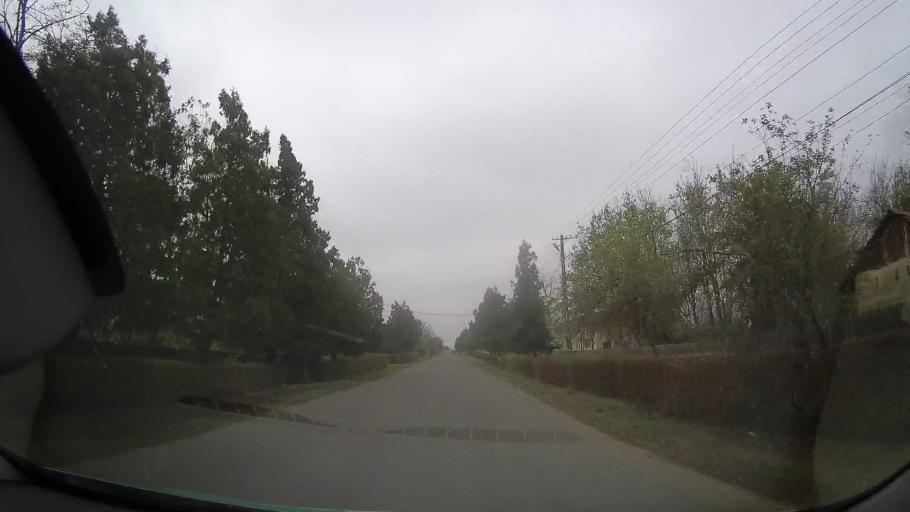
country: RO
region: Buzau
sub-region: Comuna Scutelnici
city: Scutelnici
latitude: 44.8473
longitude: 26.9166
